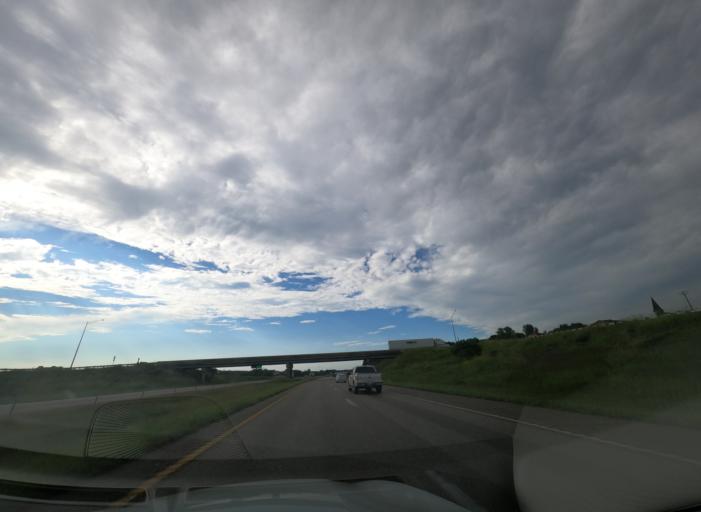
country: US
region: Missouri
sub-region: Sainte Genevieve County
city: Sainte Genevieve
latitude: 38.0050
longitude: -90.2221
